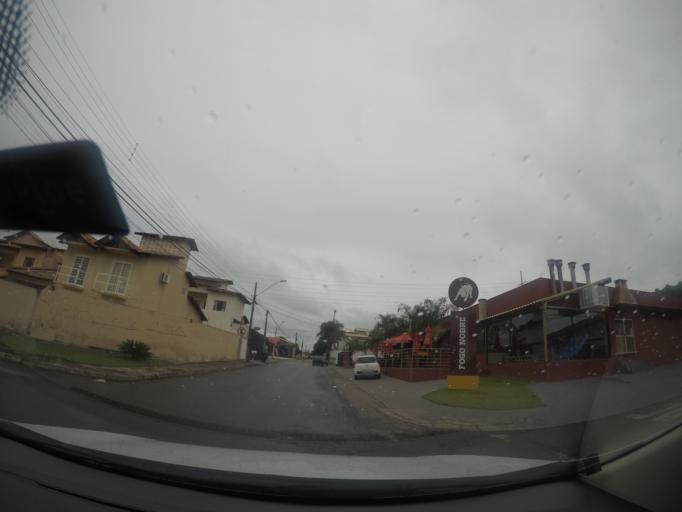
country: BR
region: Goias
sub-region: Goiania
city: Goiania
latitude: -16.7255
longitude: -49.3015
